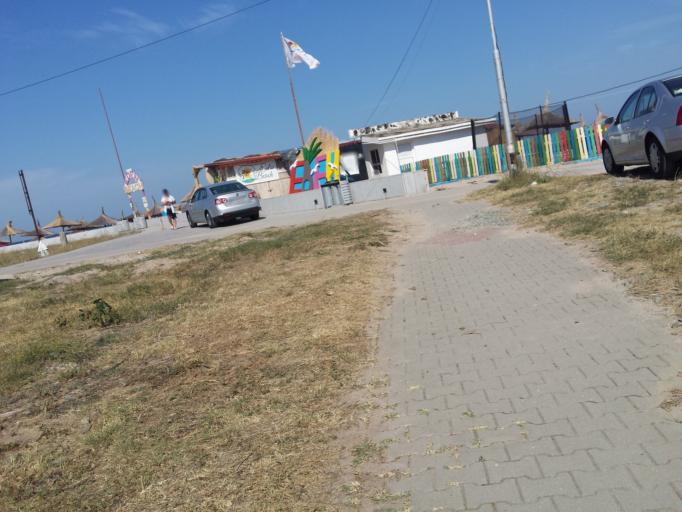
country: RO
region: Constanta
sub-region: Comuna Douazeci si Trei August
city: Douazeci si Trei August
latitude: 43.8627
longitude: 28.6053
